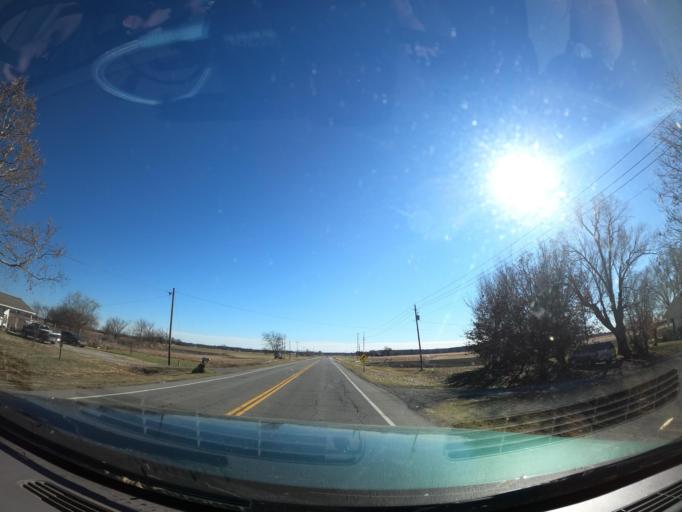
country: US
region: Oklahoma
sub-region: Muskogee County
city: Haskell
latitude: 35.7995
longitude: -95.6705
